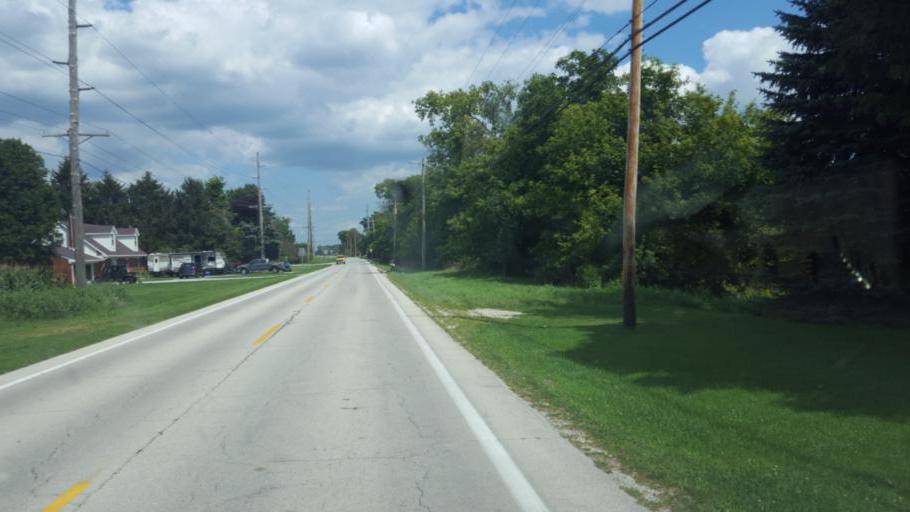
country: US
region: Ohio
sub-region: Ottawa County
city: Elmore
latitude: 41.4817
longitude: -83.2906
